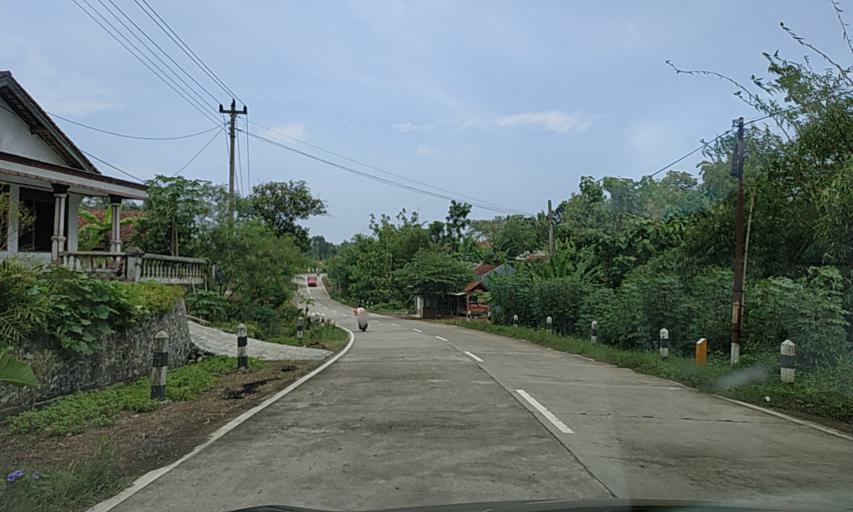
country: ID
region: Central Java
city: Ciloning
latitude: -7.4776
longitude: 108.8466
